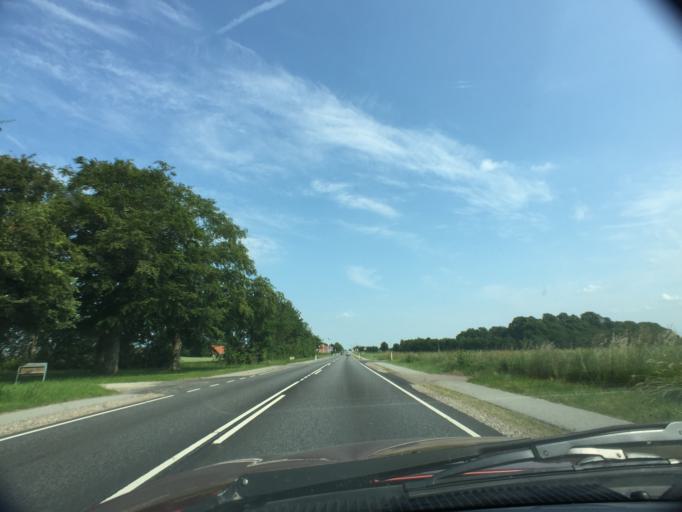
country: DK
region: Central Jutland
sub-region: Arhus Kommune
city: Sabro
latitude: 56.2131
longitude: 10.0110
